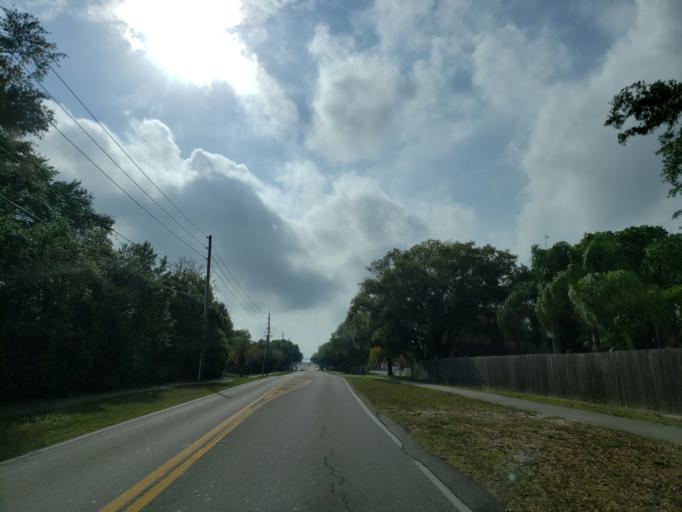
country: US
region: Florida
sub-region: Pinellas County
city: Palm Harbor
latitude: 28.0936
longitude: -82.7326
